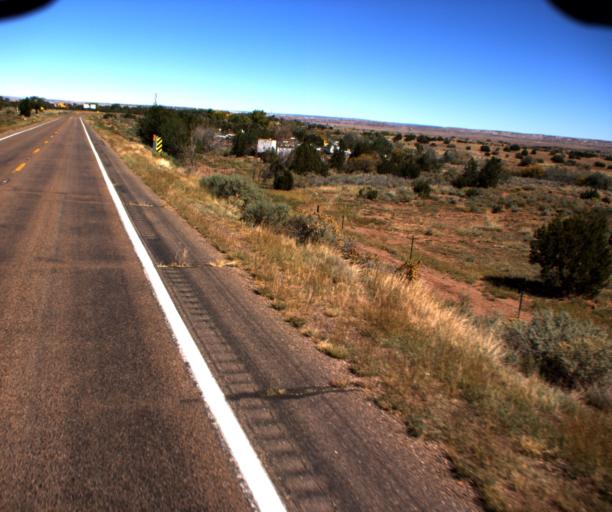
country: US
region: Arizona
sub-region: Apache County
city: Saint Johns
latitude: 34.4808
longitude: -109.3845
